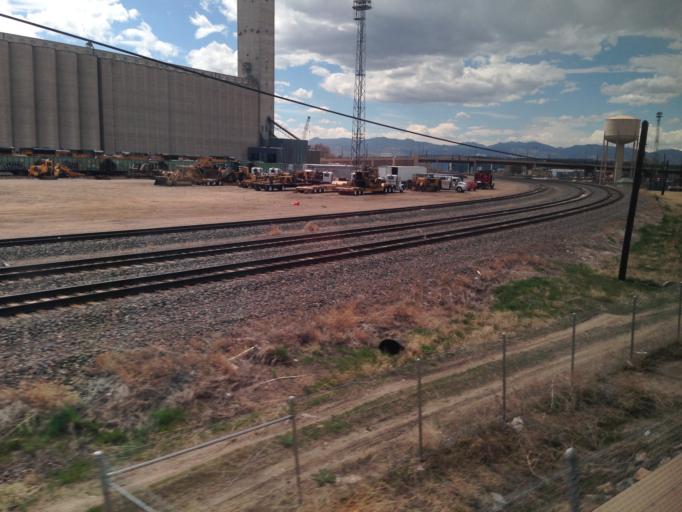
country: US
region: Colorado
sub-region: Adams County
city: Twin Lakes
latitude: 39.8029
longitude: -105.0013
